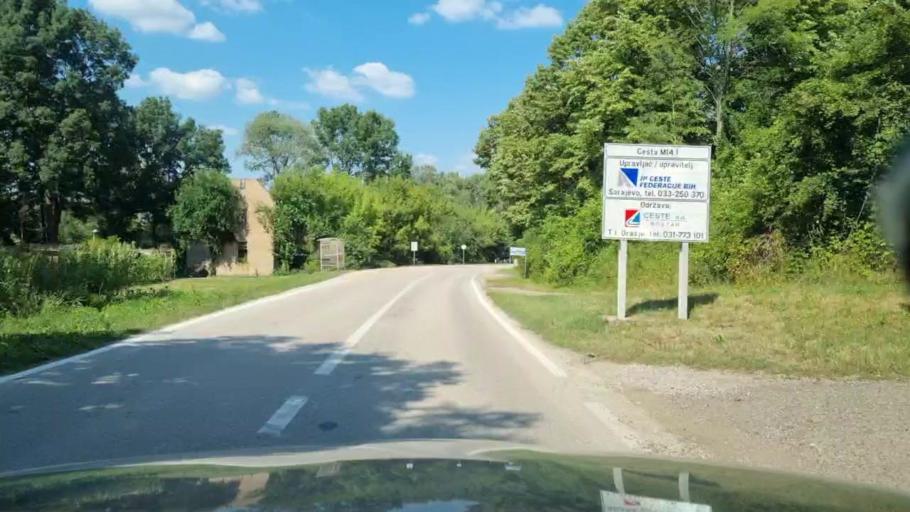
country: HR
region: Brodsko-Posavska
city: Garcin
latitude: 45.0777
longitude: 18.1987
